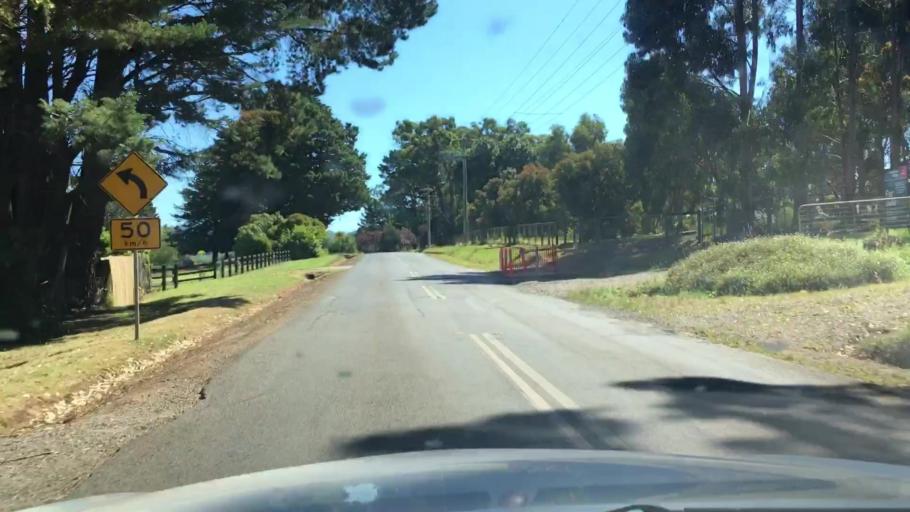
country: AU
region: Victoria
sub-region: Yarra Ranges
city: Mount Evelyn
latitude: -37.8124
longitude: 145.4247
